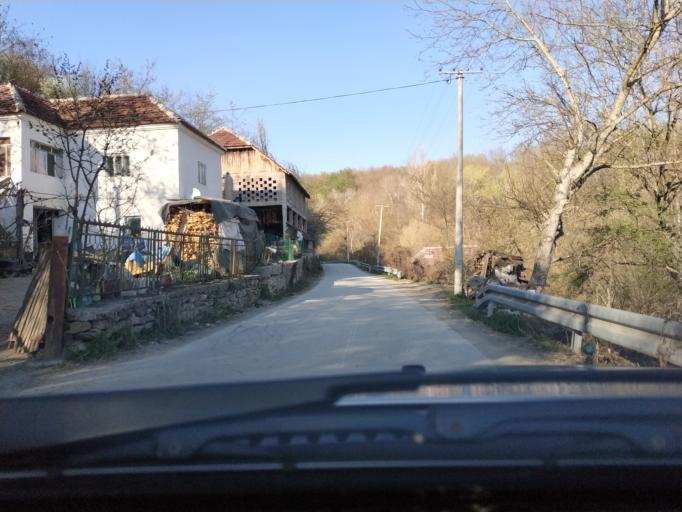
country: RS
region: Central Serbia
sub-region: Nisavski Okrug
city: Aleksinac
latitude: 43.5347
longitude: 21.8034
